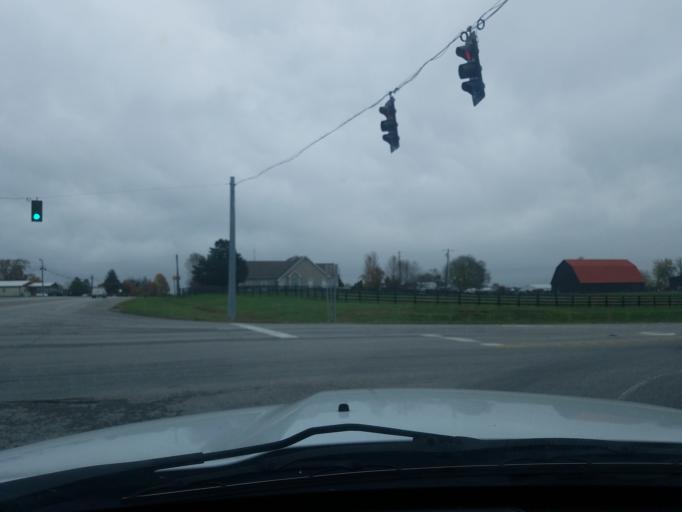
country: US
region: Kentucky
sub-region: Marion County
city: Lebanon
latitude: 37.5561
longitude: -85.2832
